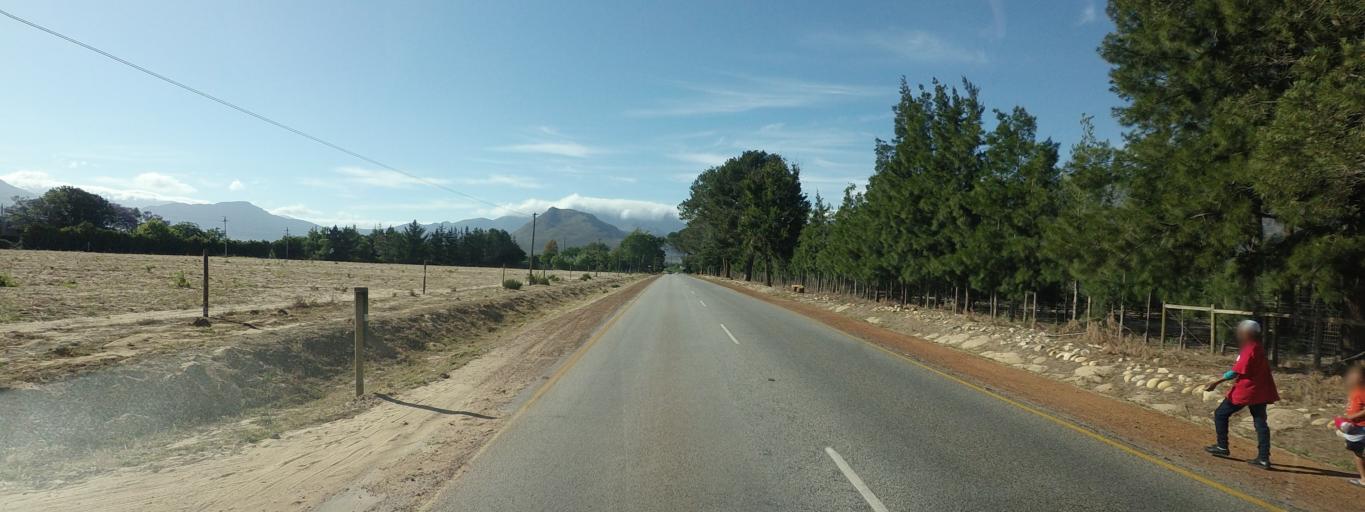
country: ZA
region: Western Cape
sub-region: Cape Winelands District Municipality
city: Paarl
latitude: -33.8686
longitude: 19.0424
